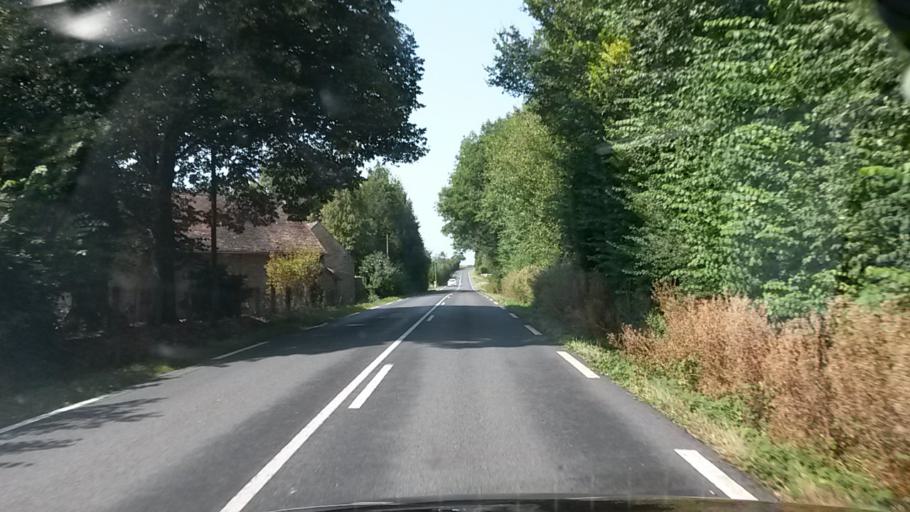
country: FR
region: Lower Normandy
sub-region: Departement de l'Orne
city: Conde-sur-Sarthe
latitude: 48.4182
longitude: -0.0127
